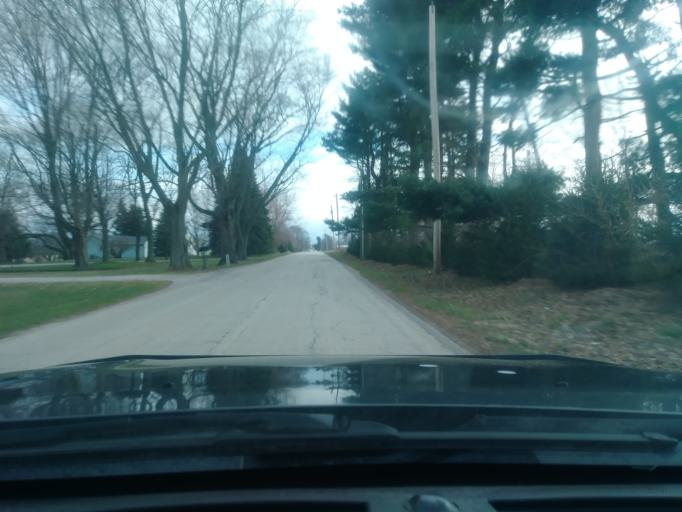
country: US
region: Indiana
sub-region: LaPorte County
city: LaPorte
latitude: 41.5739
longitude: -86.7982
